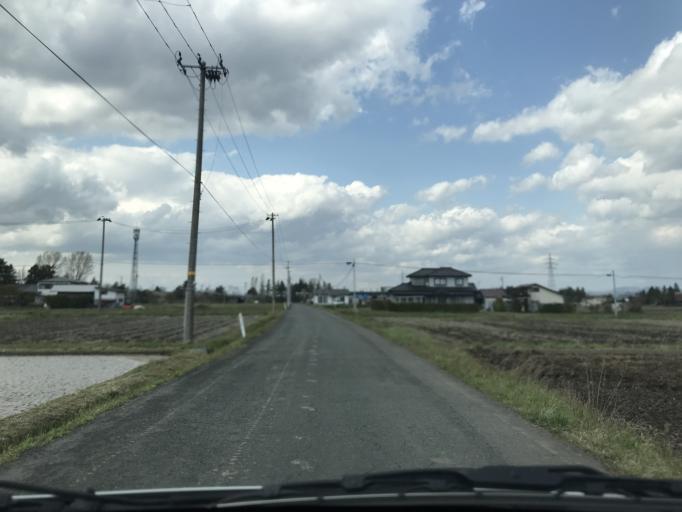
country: JP
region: Iwate
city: Mizusawa
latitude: 39.1682
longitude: 141.1207
